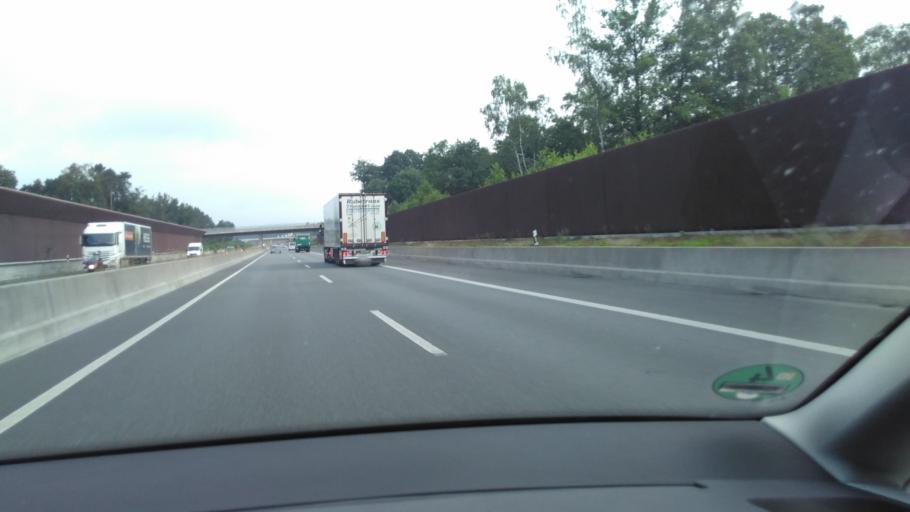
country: DE
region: North Rhine-Westphalia
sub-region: Regierungsbezirk Detmold
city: Verl
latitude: 51.9534
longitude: 8.5053
